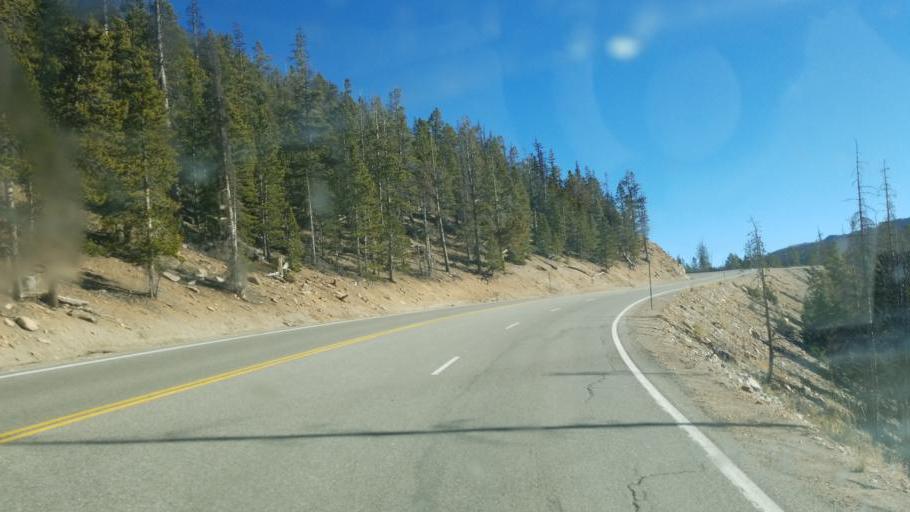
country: US
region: Colorado
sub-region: Chaffee County
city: Salida
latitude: 38.4858
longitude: -106.3314
